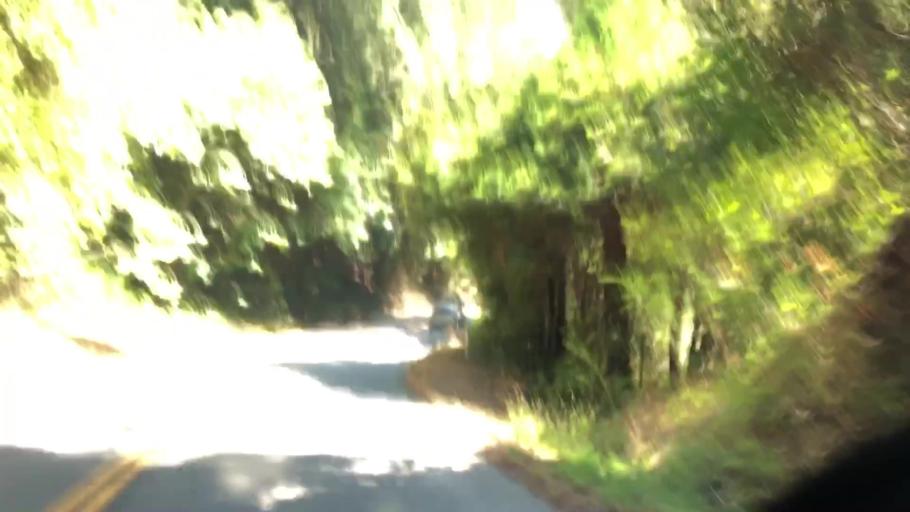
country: US
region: California
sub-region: Santa Cruz County
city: Corralitos
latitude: 37.0270
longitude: -121.8201
